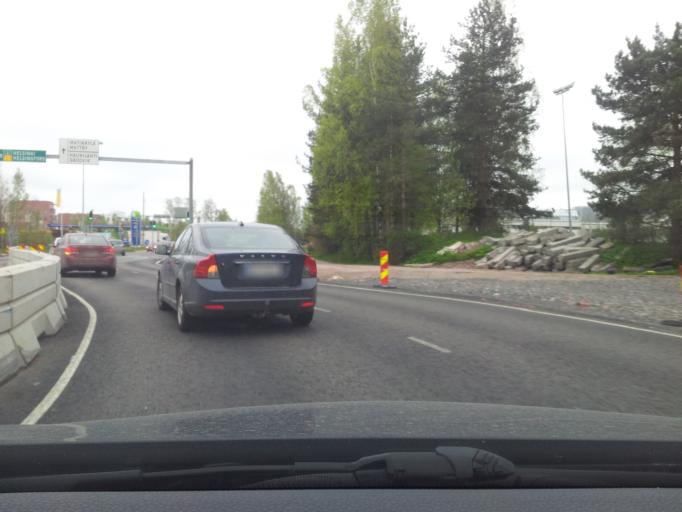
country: FI
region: Uusimaa
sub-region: Helsinki
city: Koukkuniemi
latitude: 60.1655
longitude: 24.7523
